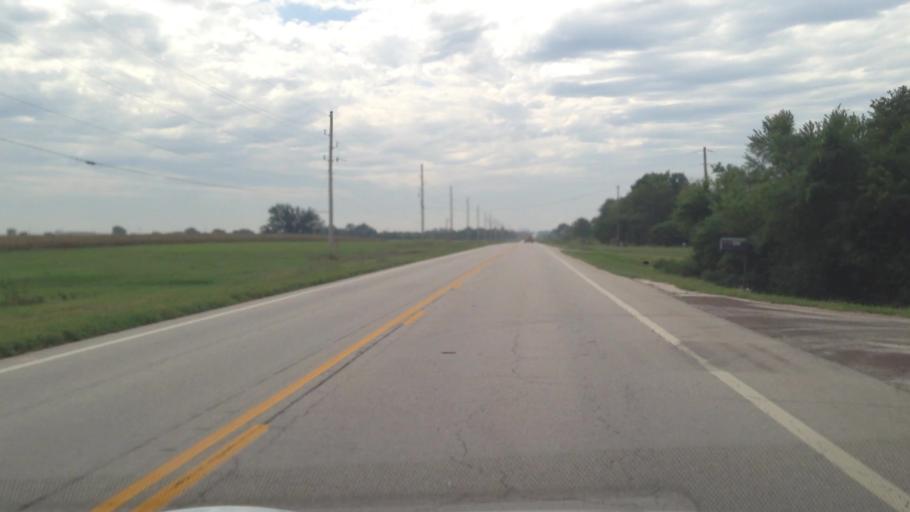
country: US
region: Kansas
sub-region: Allen County
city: Iola
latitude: 37.9580
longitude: -95.1701
